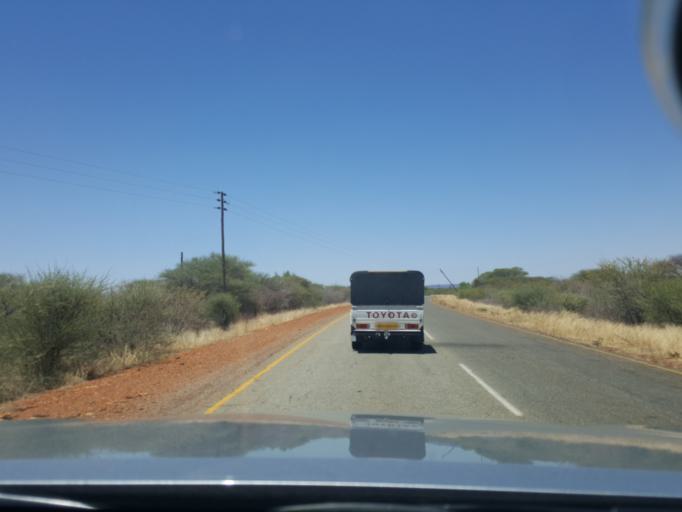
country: BW
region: South East
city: Otse
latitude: -25.1049
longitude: 25.9601
